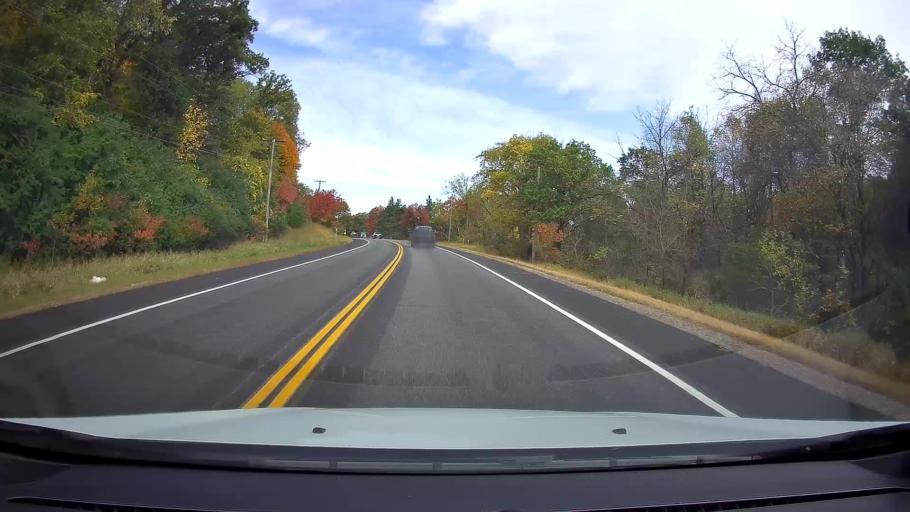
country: US
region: Minnesota
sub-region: Washington County
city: Scandia
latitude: 45.1766
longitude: -92.7657
